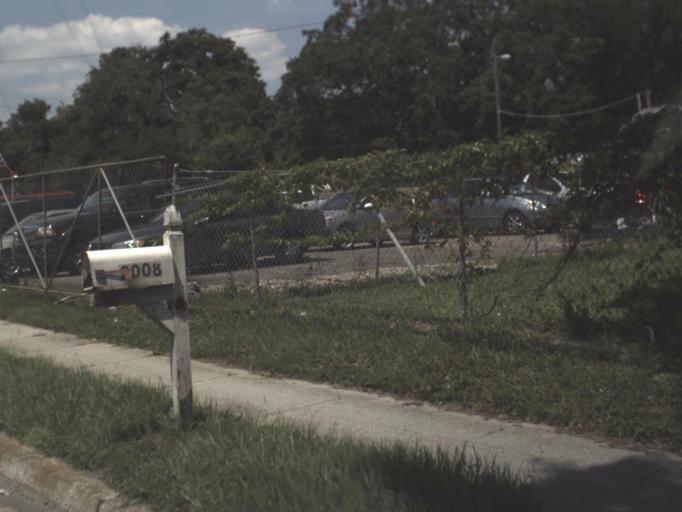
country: US
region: Florida
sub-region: Hillsborough County
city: Palm River-Clair Mel
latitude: 27.9299
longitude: -82.4018
